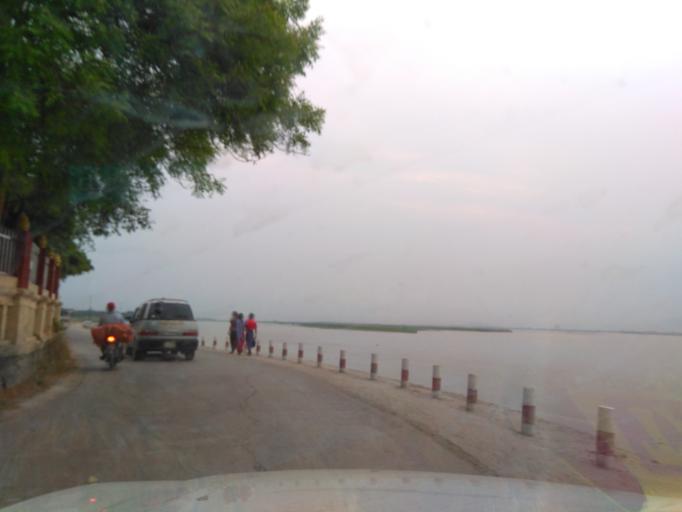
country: MM
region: Sagain
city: Sagaing
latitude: 21.9035
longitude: 96.0014
